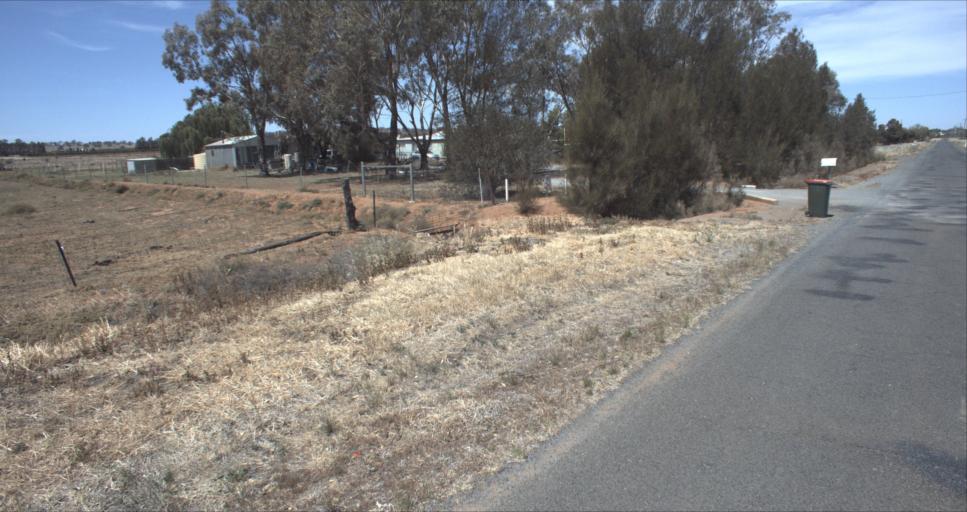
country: AU
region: New South Wales
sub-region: Leeton
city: Leeton
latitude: -34.5999
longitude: 146.4272
